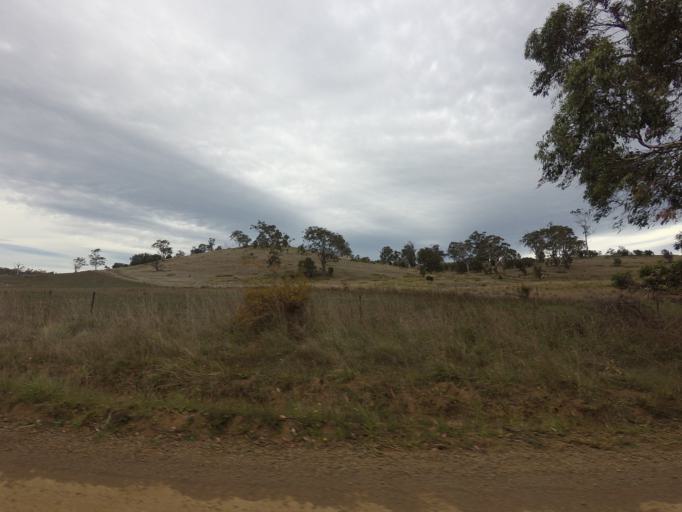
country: AU
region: Tasmania
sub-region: Derwent Valley
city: New Norfolk
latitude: -42.5634
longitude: 146.9281
